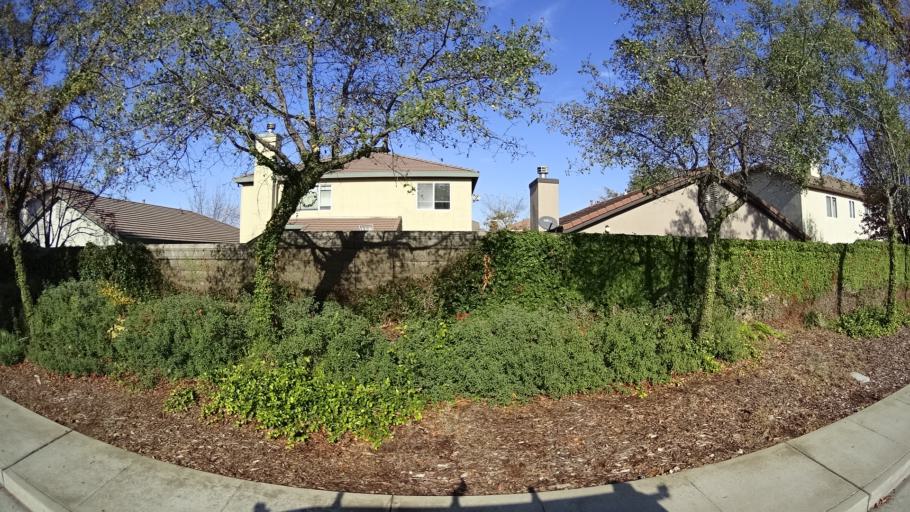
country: US
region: California
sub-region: Sacramento County
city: Antelope
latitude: 38.6885
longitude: -121.3105
